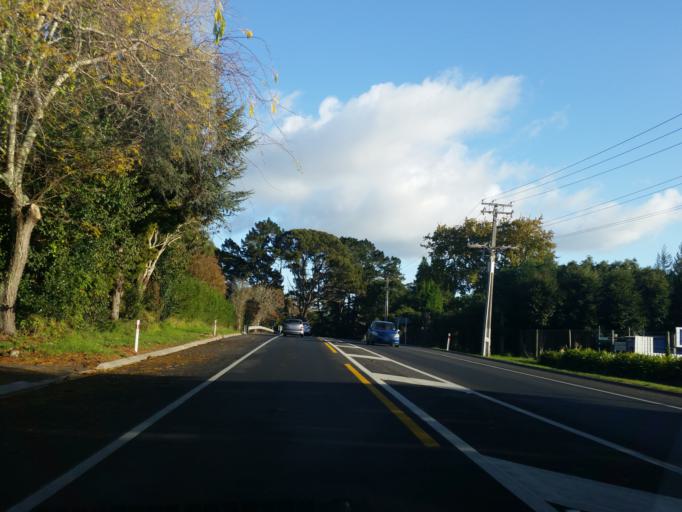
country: NZ
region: Bay of Plenty
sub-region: Tauranga City
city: Tauranga
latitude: -37.7007
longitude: 176.0800
